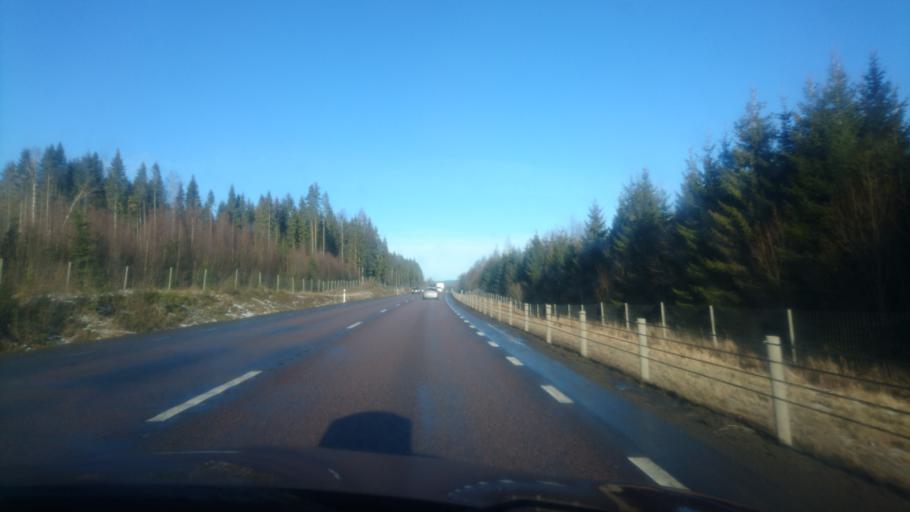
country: SE
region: Vaermland
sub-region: Sunne Kommun
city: Sunne
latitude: 59.7520
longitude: 13.1197
